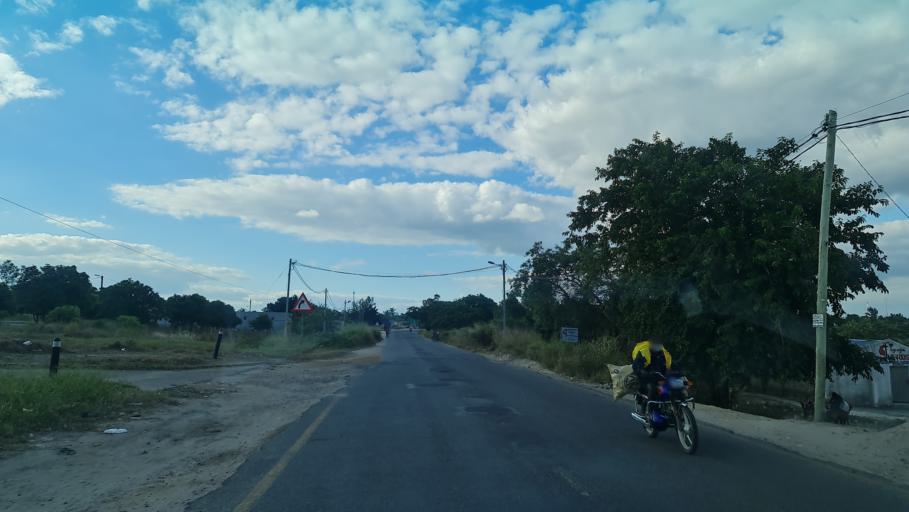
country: MZ
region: Manica
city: Chimoio
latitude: -19.2146
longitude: 33.9235
